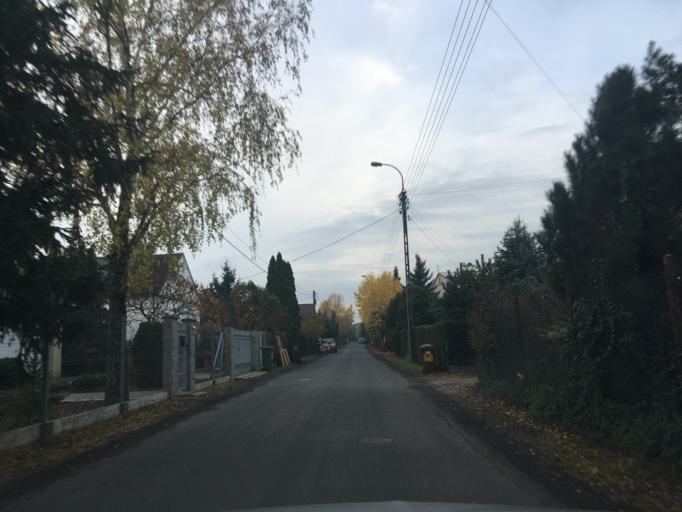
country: PL
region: Masovian Voivodeship
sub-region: Powiat pruszkowski
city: Brwinow
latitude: 52.1423
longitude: 20.7321
